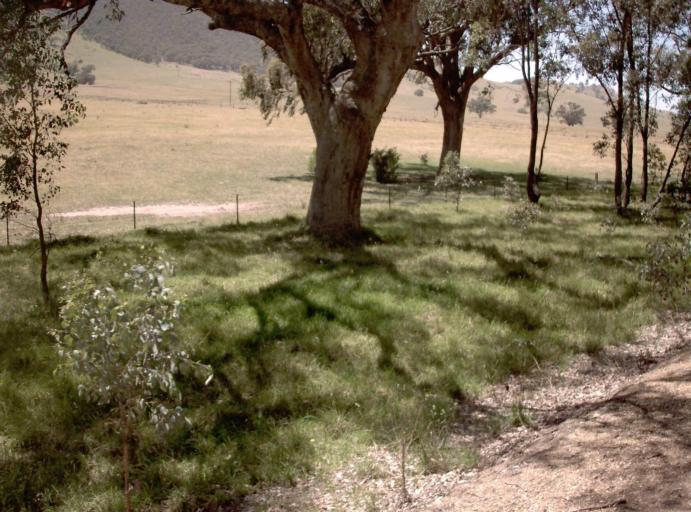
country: AU
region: Victoria
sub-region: East Gippsland
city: Bairnsdale
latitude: -37.3311
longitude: 147.7813
